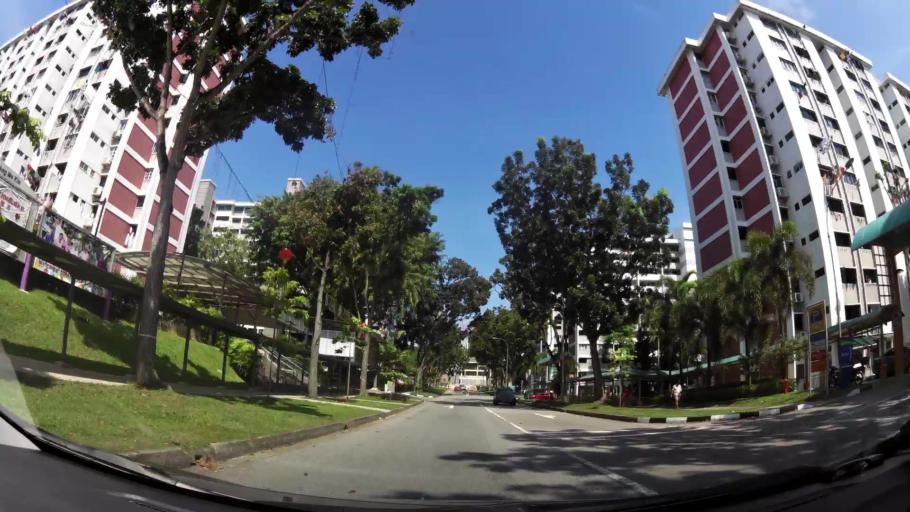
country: SG
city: Singapore
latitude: 1.3816
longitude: 103.8407
